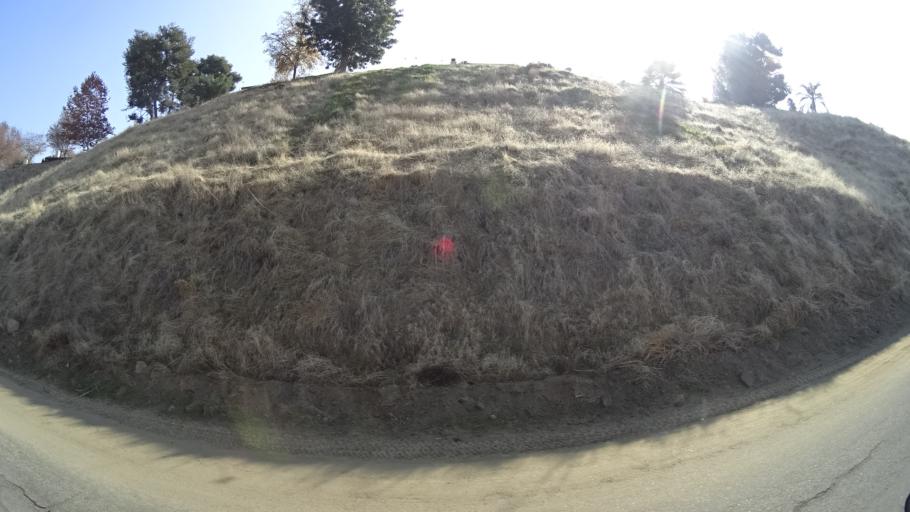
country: US
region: California
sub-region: Kern County
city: Oildale
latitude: 35.4330
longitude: -118.8766
